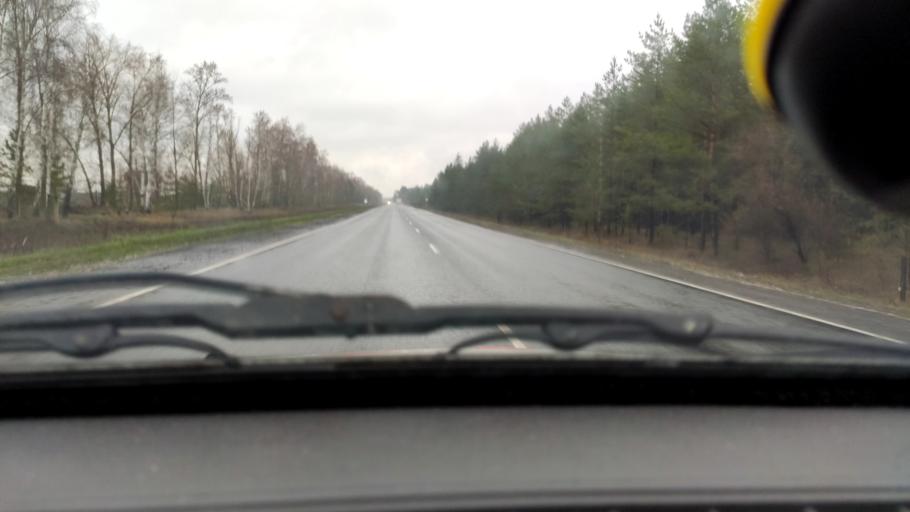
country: RU
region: Samara
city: Povolzhskiy
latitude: 53.6152
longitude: 49.6279
